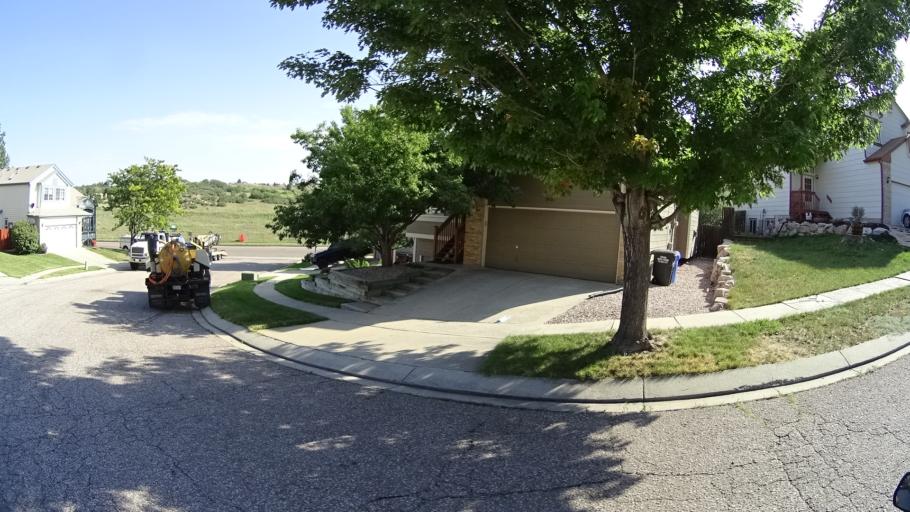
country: US
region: Colorado
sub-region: El Paso County
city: Air Force Academy
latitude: 38.9473
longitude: -104.7787
